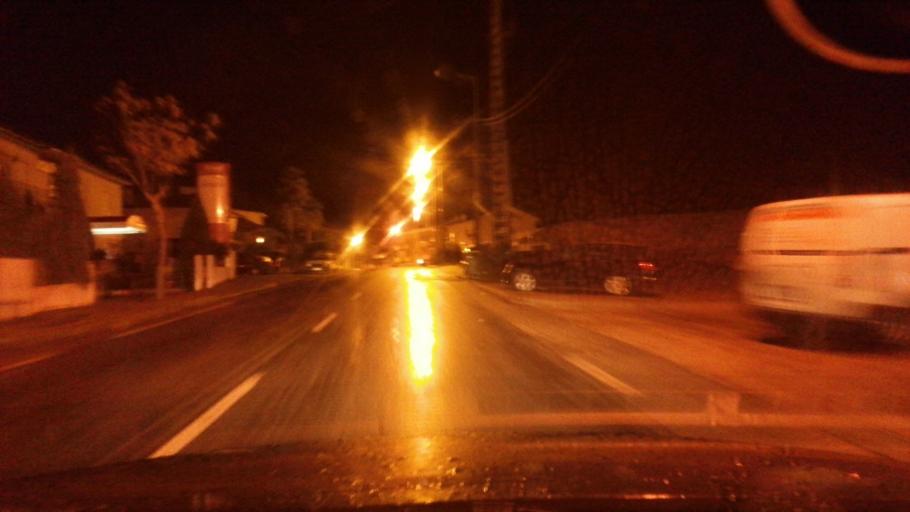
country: PT
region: Viseu
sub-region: Moimenta da Beira
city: Moimenta da Beira
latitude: 40.9716
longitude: -7.6067
